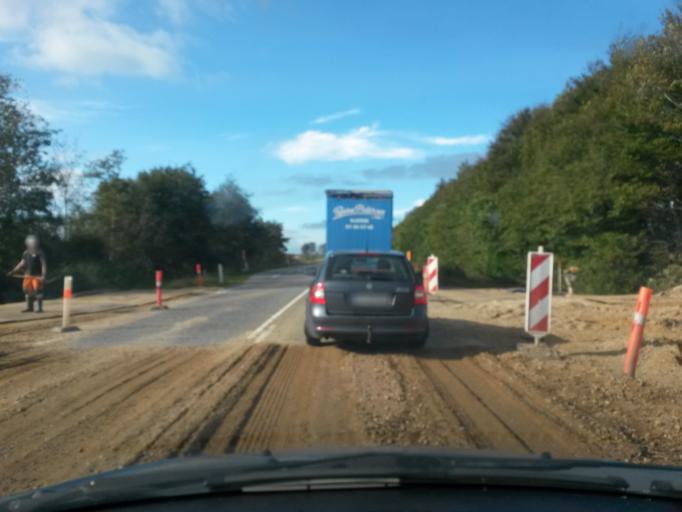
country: DK
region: Central Jutland
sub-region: Herning Kommune
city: Avlum
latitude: 56.2948
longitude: 8.7261
